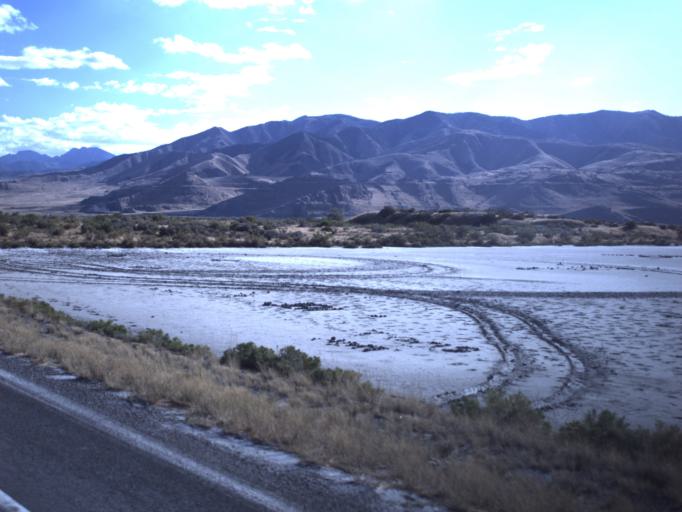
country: US
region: Utah
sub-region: Tooele County
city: Grantsville
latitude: 40.7070
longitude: -112.5302
